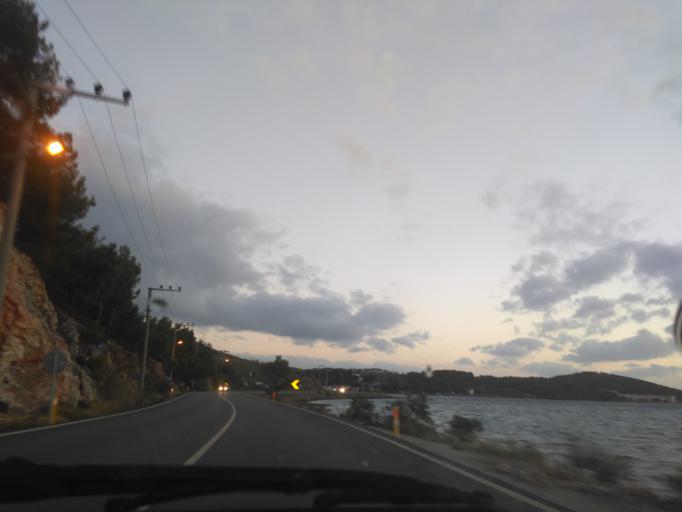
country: TR
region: Balikesir
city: Ayvalik
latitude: 39.2895
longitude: 26.6709
